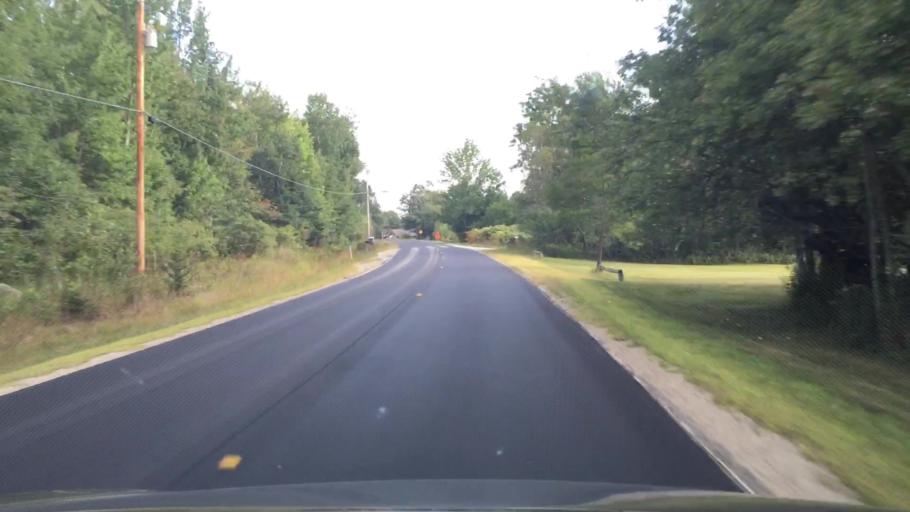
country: US
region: Maine
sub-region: Hancock County
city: Orland
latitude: 44.5485
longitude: -68.6208
